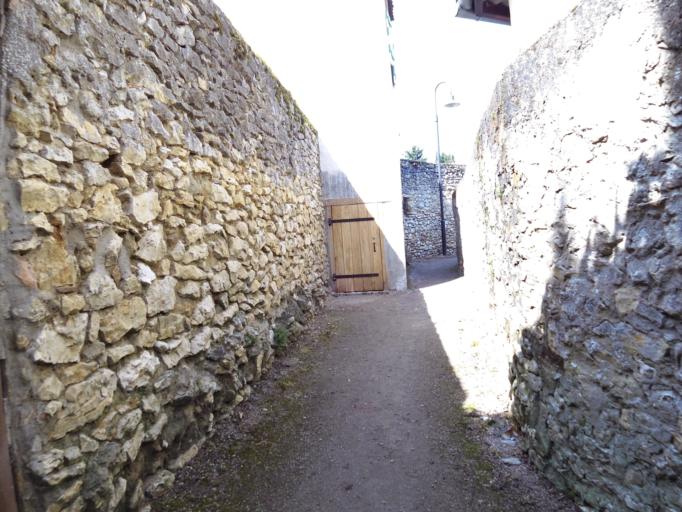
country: DE
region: Rheinland-Pfalz
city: Westhofen
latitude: 49.7016
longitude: 8.2441
